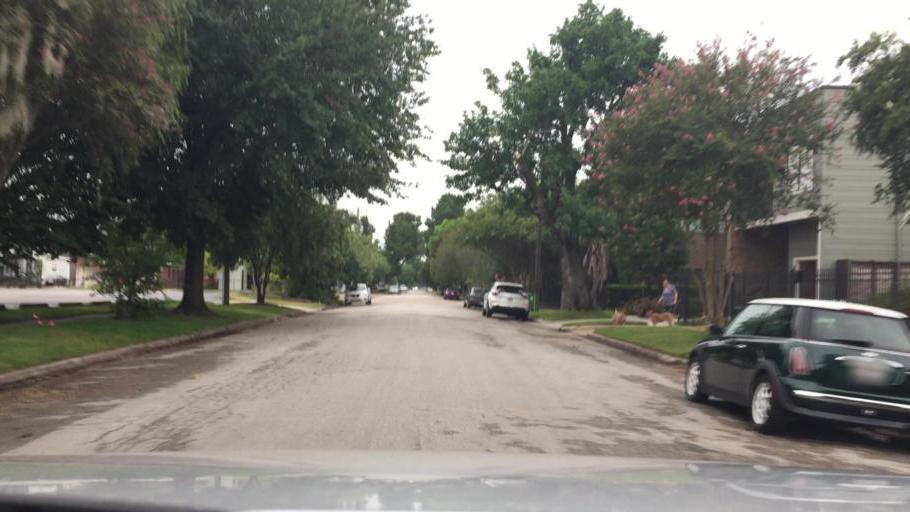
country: US
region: Texas
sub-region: Harris County
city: Houston
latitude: 29.7915
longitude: -95.3920
